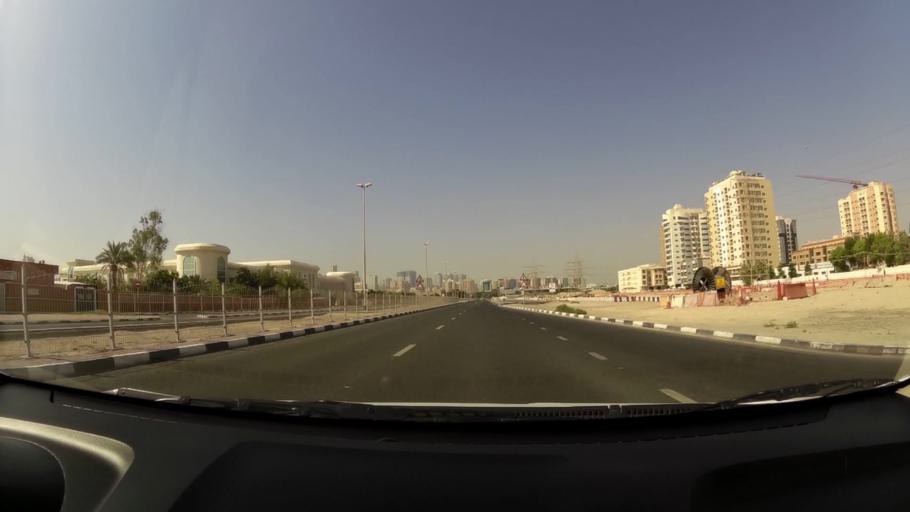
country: AE
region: Ash Shariqah
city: Sharjah
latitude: 25.2796
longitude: 55.3699
